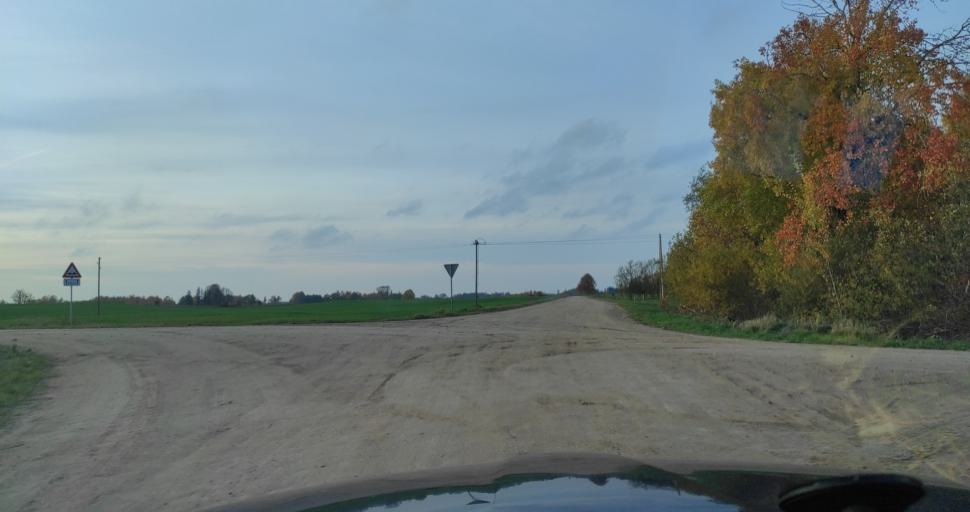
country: LV
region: Skrunda
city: Skrunda
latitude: 56.6395
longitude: 21.8089
